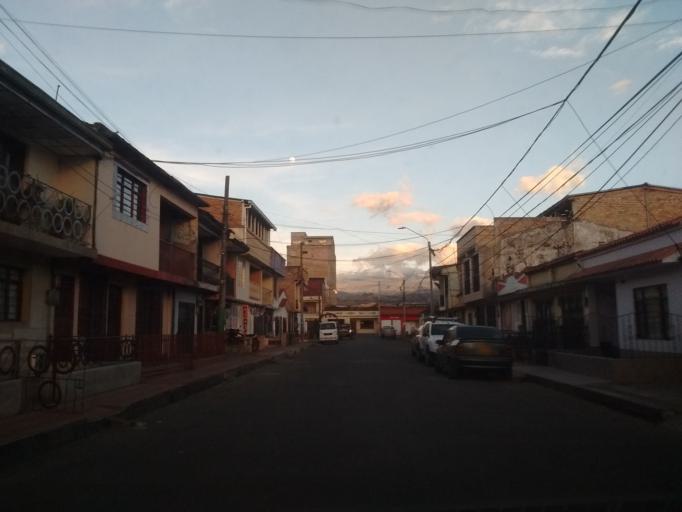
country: CO
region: Cauca
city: Popayan
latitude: 2.4460
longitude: -76.6191
